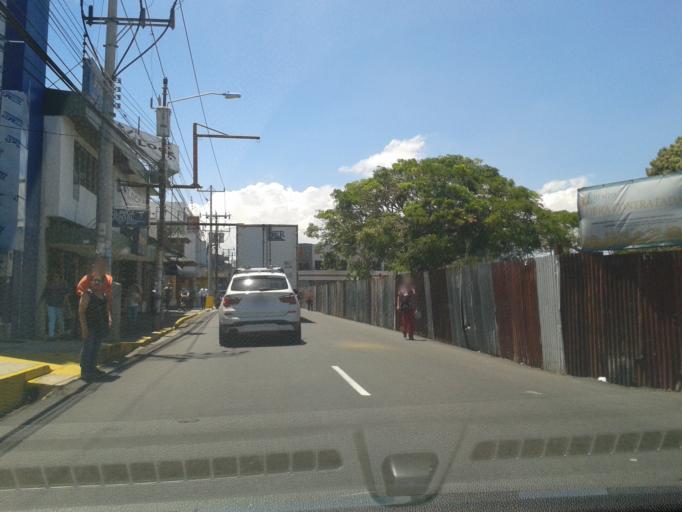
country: CR
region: Heredia
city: Heredia
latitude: 9.9966
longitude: -84.1202
